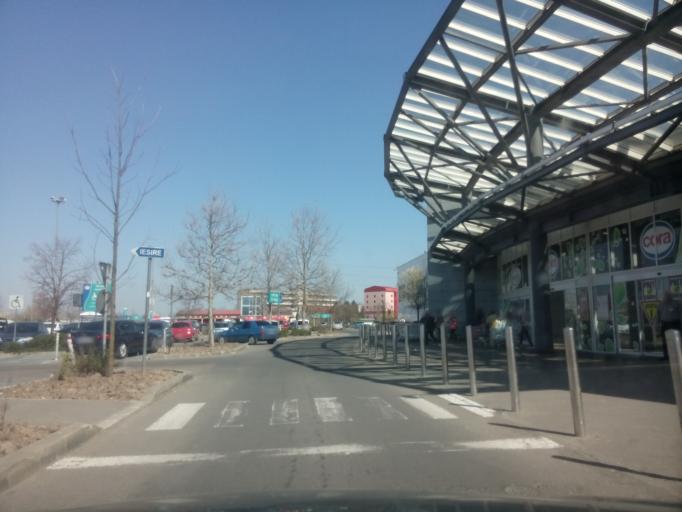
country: RO
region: Ilfov
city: Dobroesti
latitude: 44.4384
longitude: 26.1869
